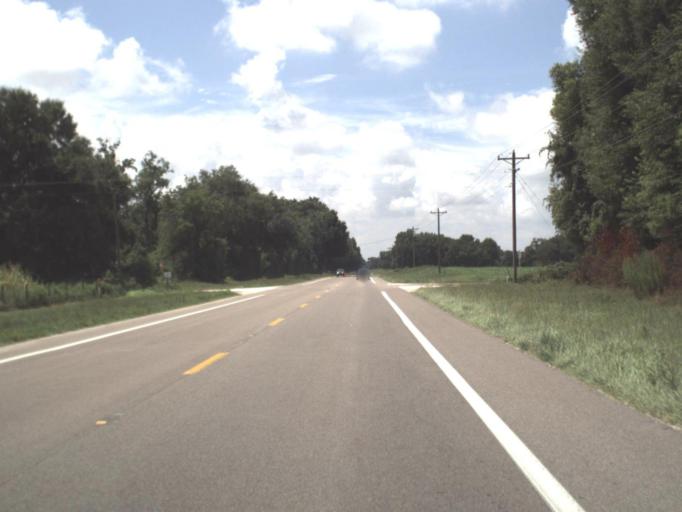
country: US
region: Florida
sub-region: Gilchrist County
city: Trenton
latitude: 29.7055
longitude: -82.8575
